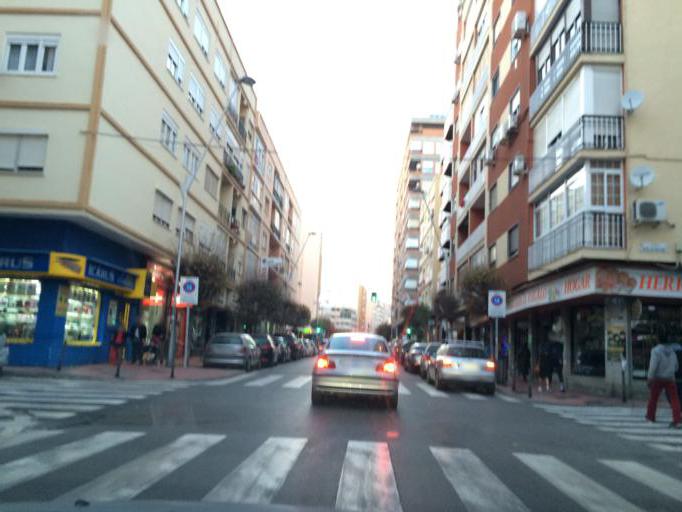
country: ES
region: Andalusia
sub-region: Provincia de Almeria
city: Almeria
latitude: 36.8382
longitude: -2.4574
